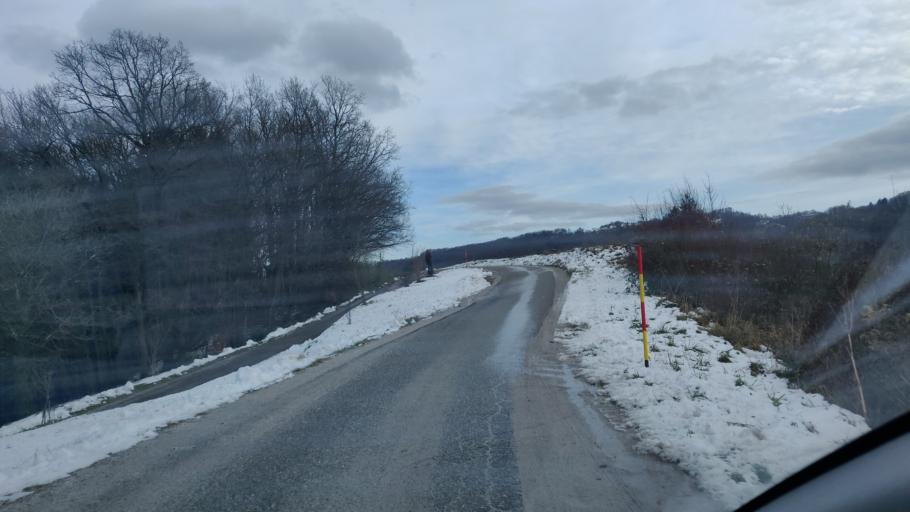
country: SI
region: Makole
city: Makole
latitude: 46.3250
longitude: 15.6667
